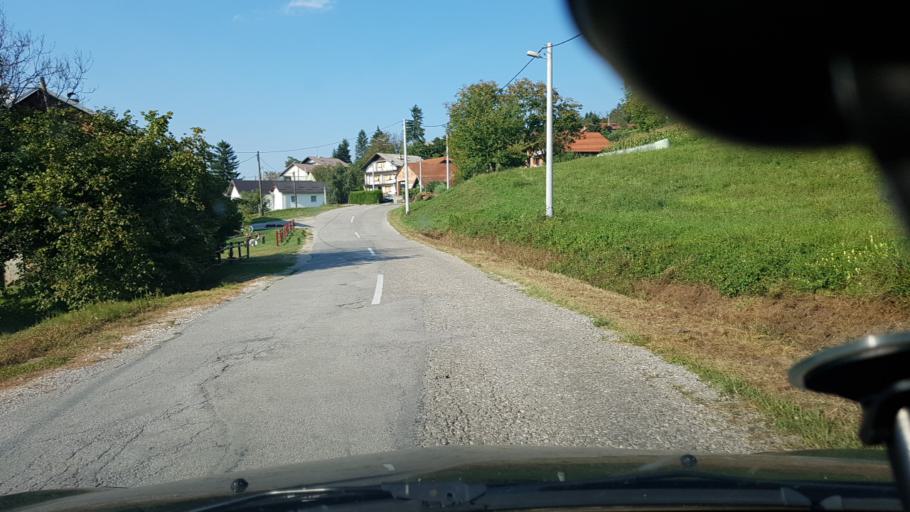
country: HR
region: Zagrebacka
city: Pojatno
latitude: 45.9232
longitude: 15.7169
